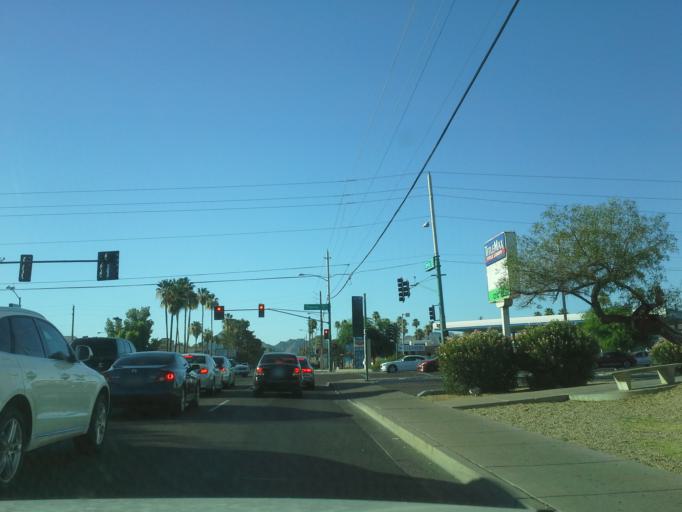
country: US
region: Arizona
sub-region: Maricopa County
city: Phoenix
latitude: 33.4800
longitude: -112.0128
